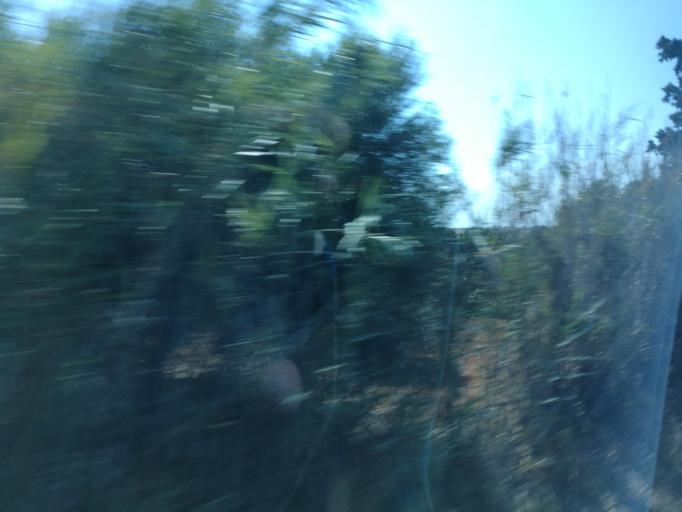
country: CY
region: Ammochostos
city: Avgorou
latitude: 35.0676
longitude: 33.8309
